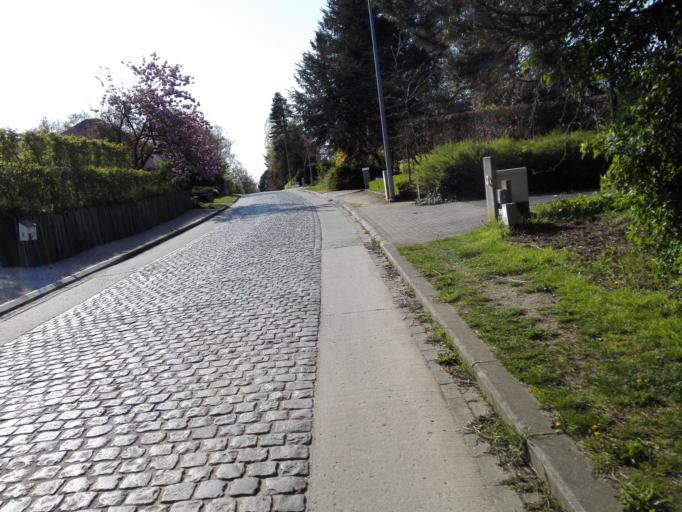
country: BE
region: Flanders
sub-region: Provincie Vlaams-Brabant
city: Leuven
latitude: 50.8729
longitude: 4.7425
